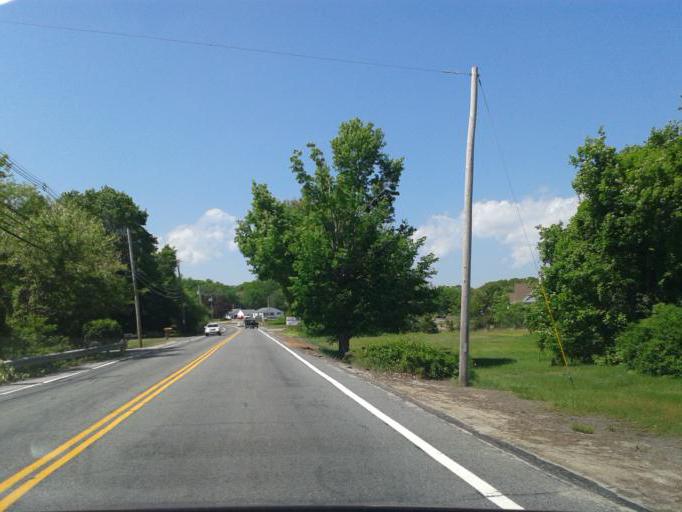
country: US
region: Rhode Island
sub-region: Washington County
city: Hope Valley
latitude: 41.5059
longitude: -71.6806
